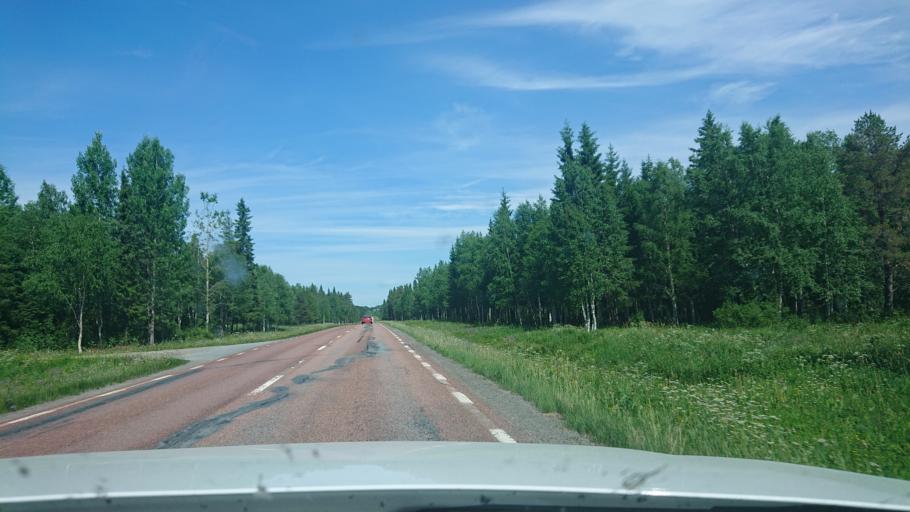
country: SE
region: Jaemtland
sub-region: Stroemsunds Kommun
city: Stroemsund
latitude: 63.7978
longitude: 15.5158
